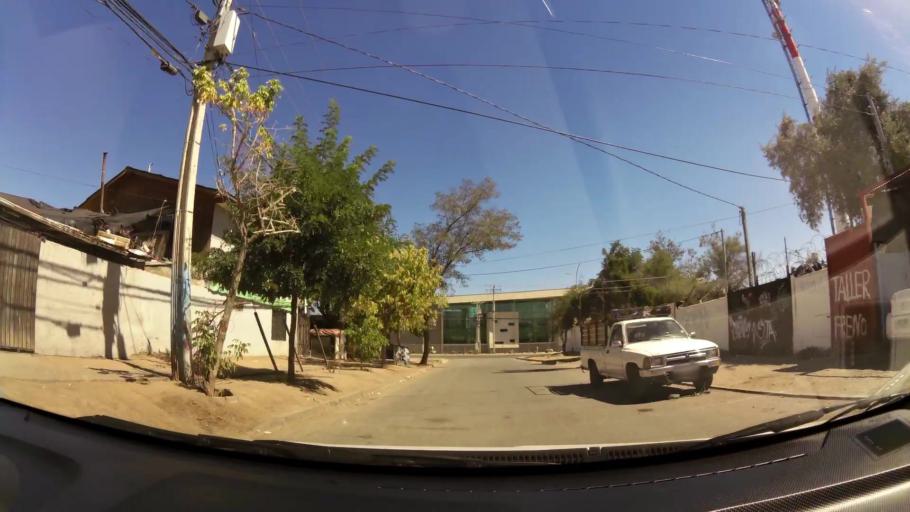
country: CL
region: O'Higgins
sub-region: Provincia de Cachapoal
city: Rancagua
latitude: -34.1641
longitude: -70.7133
